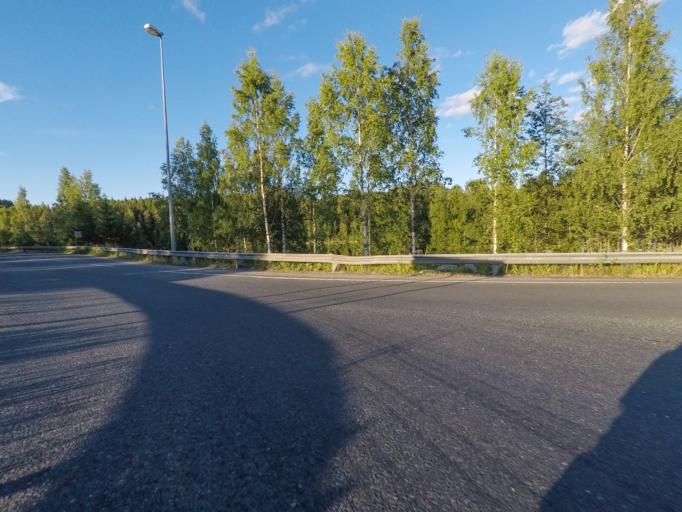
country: FI
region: Northern Savo
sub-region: Kuopio
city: Kuopio
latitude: 62.8409
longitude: 27.6075
